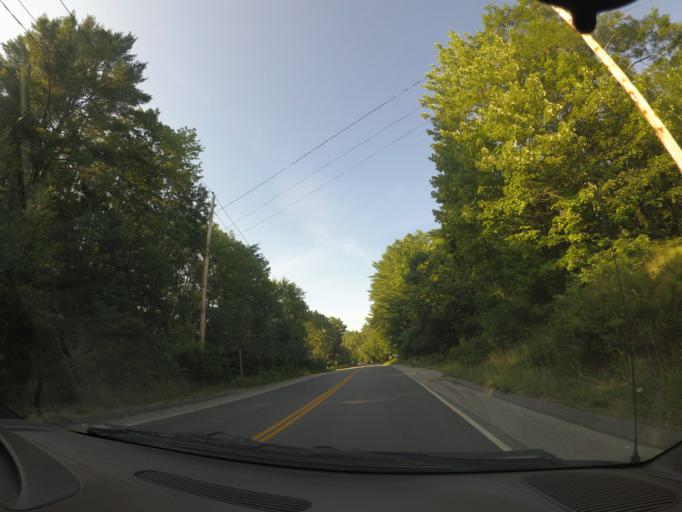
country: US
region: Maine
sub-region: Cumberland County
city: Raymond
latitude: 43.8911
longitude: -70.4598
